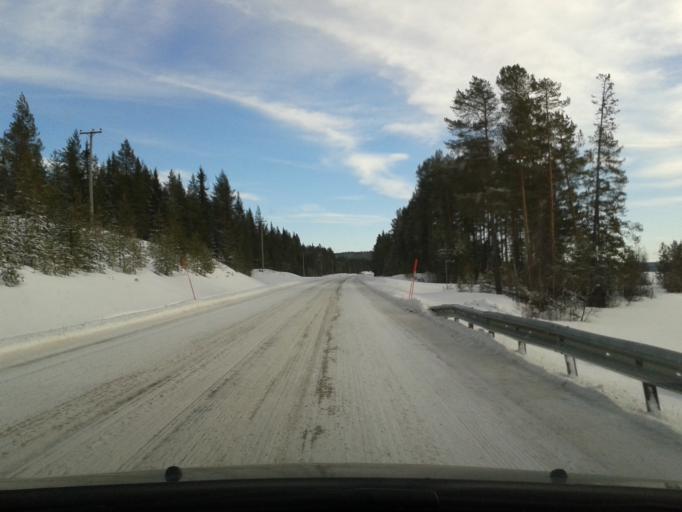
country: SE
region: Vaesterbotten
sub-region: Vilhelmina Kommun
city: Vilhelmina
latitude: 64.3880
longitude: 16.8810
